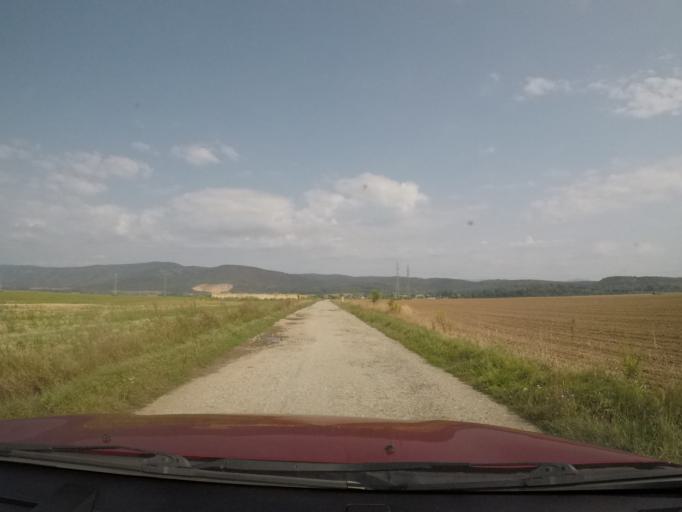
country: SK
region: Kosicky
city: Moldava nad Bodvou
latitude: 48.5950
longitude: 20.9560
